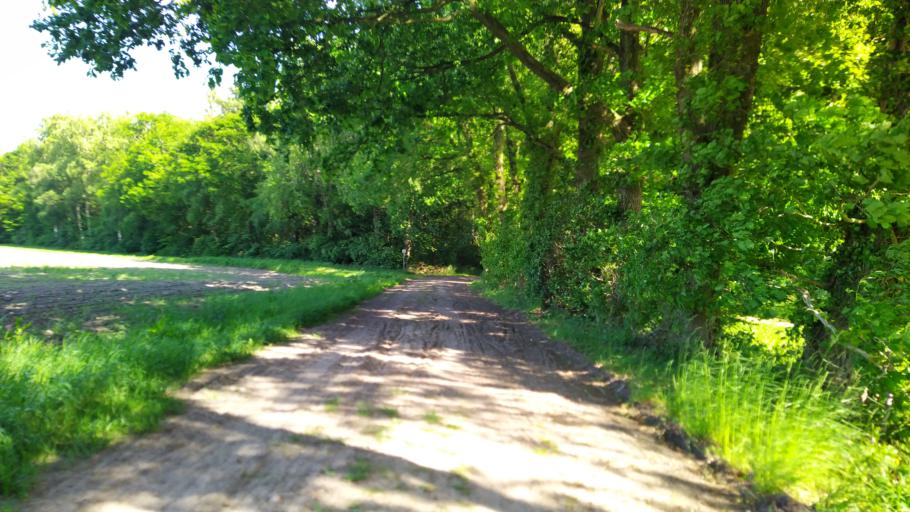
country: DE
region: Lower Saxony
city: Ahlerstedt
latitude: 53.4215
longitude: 9.4813
